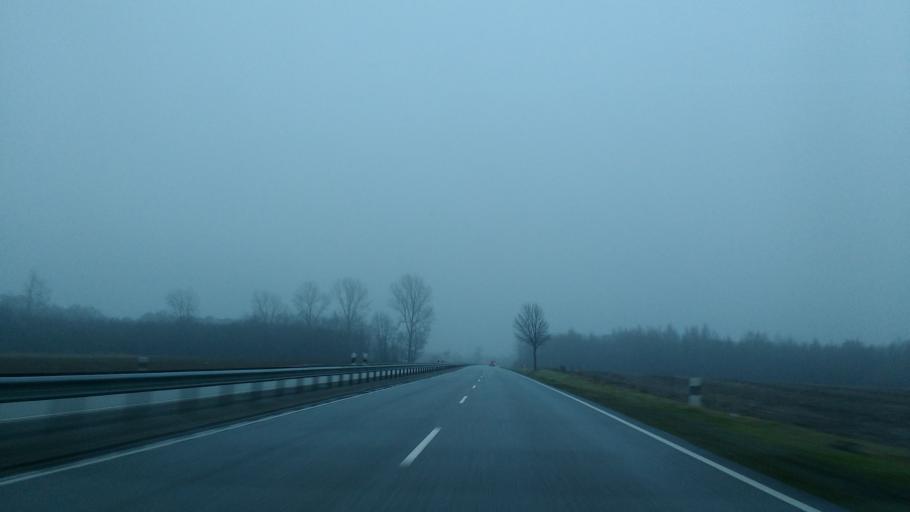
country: DE
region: Schleswig-Holstein
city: Jevenstedt
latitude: 54.2437
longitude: 9.6722
